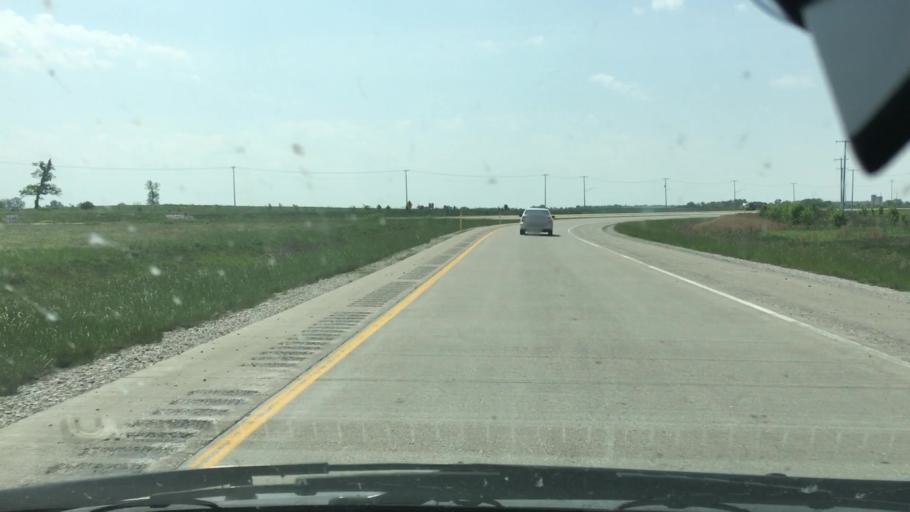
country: US
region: Indiana
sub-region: Daviess County
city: Washington
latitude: 38.6533
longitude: -87.1218
